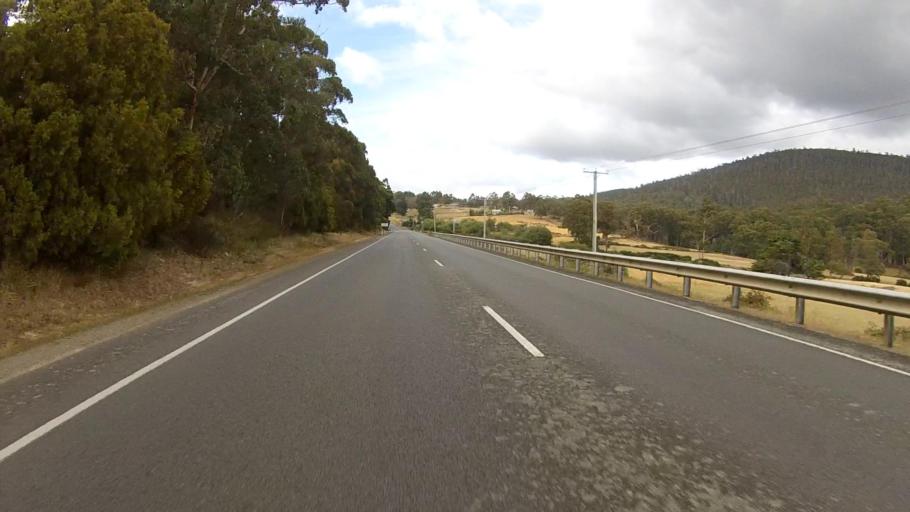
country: AU
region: Tasmania
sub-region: Kingborough
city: Kettering
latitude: -43.0823
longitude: 147.2539
